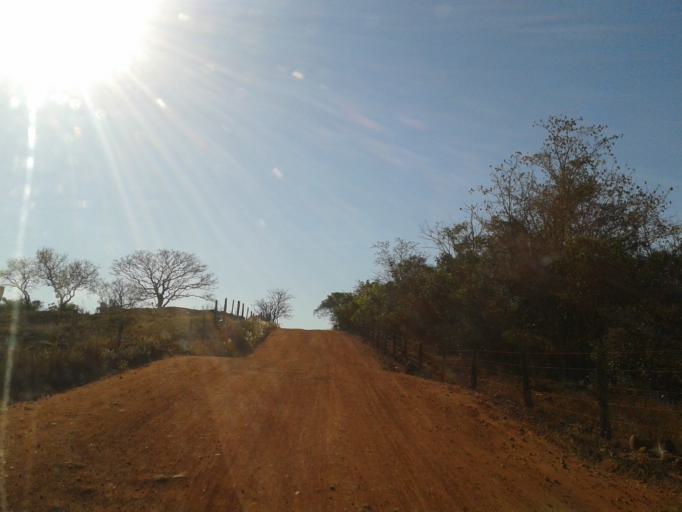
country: BR
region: Minas Gerais
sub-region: Ituiutaba
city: Ituiutaba
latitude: -18.9757
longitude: -49.4163
